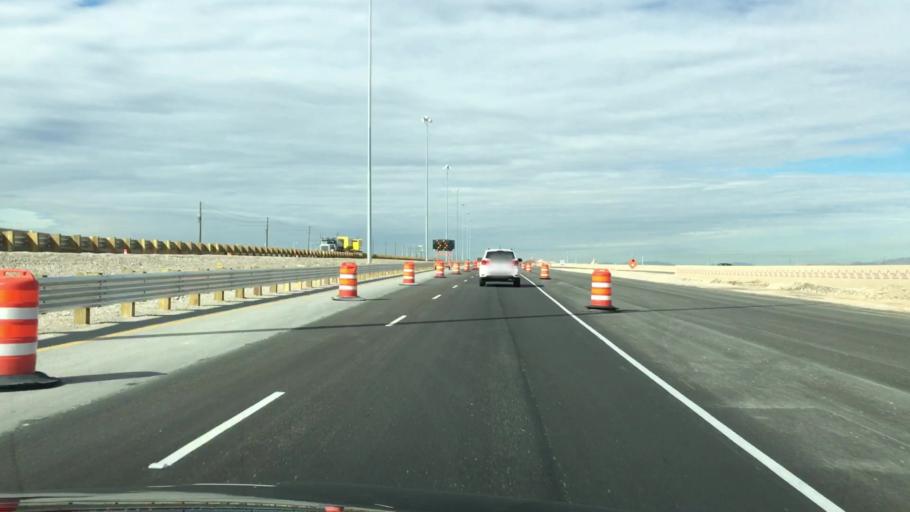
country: US
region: Nevada
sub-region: Clark County
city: Summerlin South
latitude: 36.3159
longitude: -115.3017
